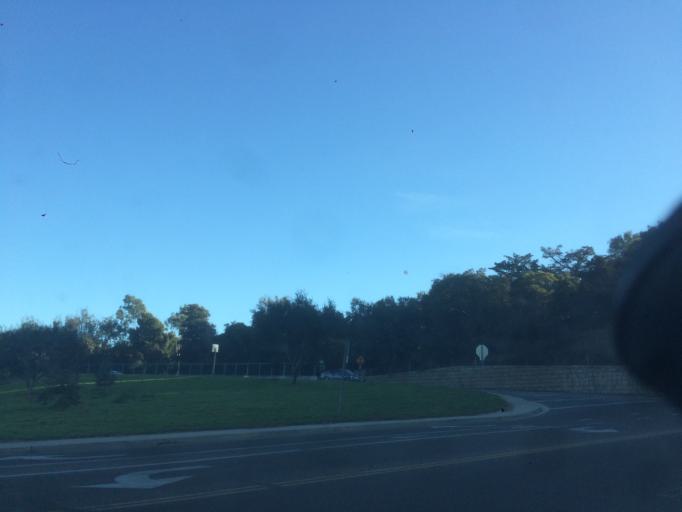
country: US
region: California
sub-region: Santa Barbara County
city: Mission Canyon
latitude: 34.4367
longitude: -119.7539
